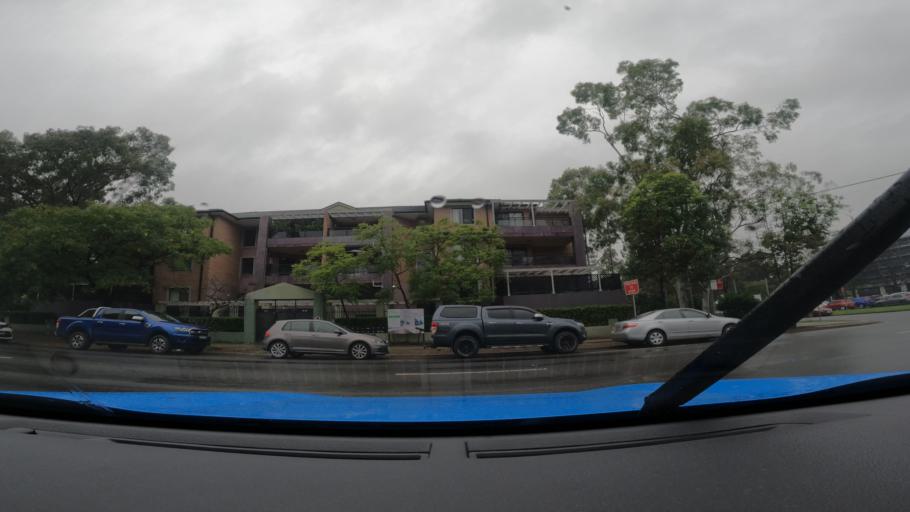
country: AU
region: New South Wales
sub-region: Penrith Municipality
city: Kingswood Park
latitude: -33.7587
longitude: 150.7161
